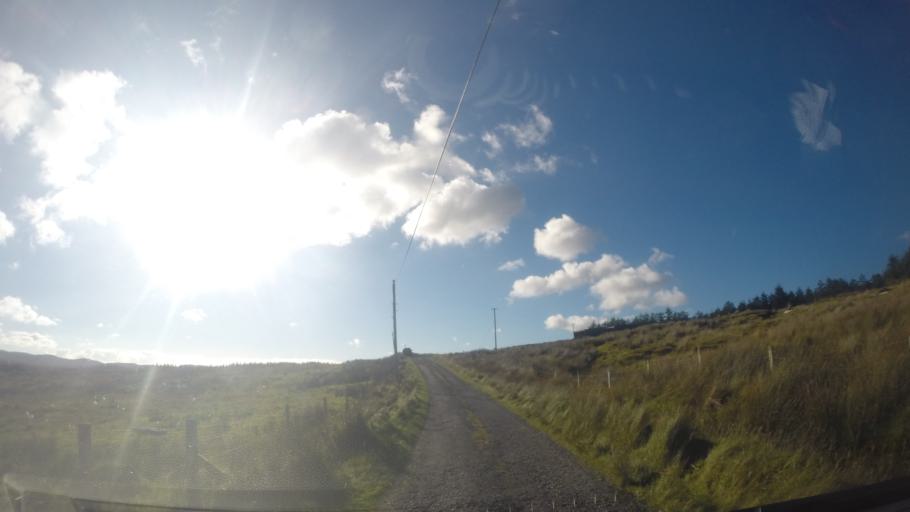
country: IE
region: Ulster
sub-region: County Donegal
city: Killybegs
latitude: 54.7232
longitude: -8.5687
